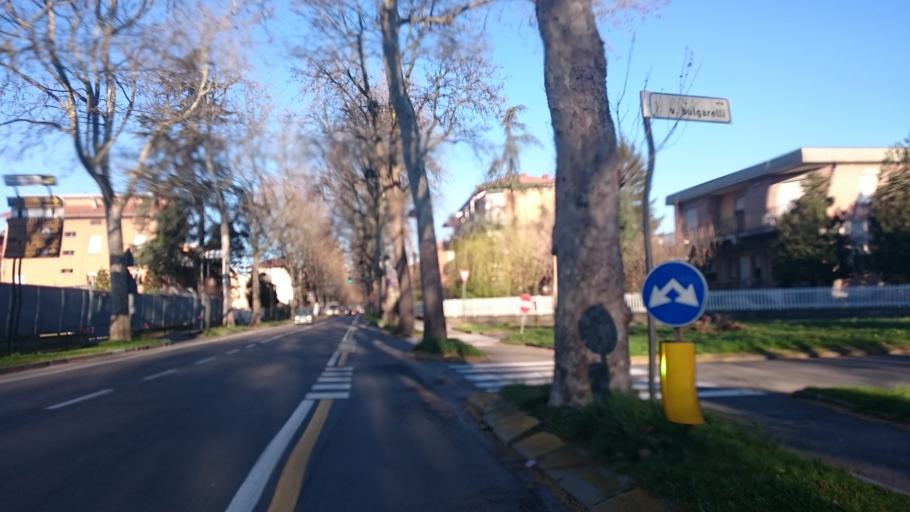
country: IT
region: Emilia-Romagna
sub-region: Provincia di Reggio Emilia
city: Reggio nell'Emilia
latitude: 44.7039
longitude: 10.6521
